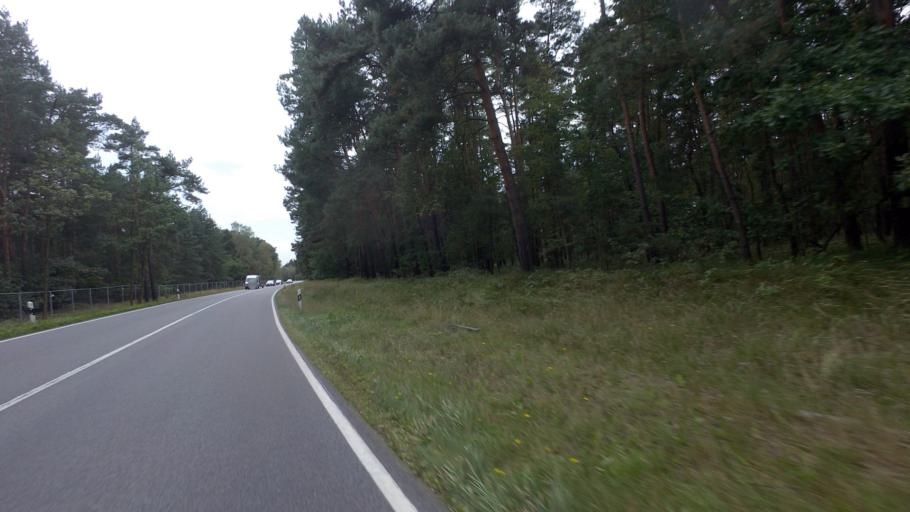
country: DE
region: Saxony
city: Wittichenau
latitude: 51.3763
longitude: 14.2917
